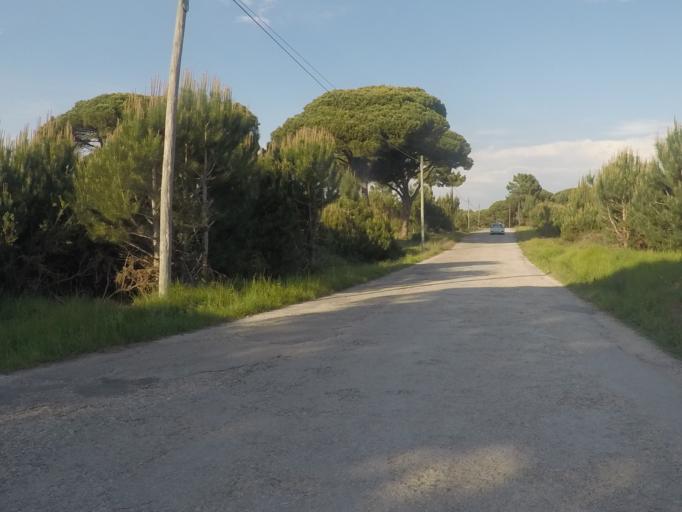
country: PT
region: Setubal
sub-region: Sesimbra
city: Sesimbra
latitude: 38.4597
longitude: -9.1851
